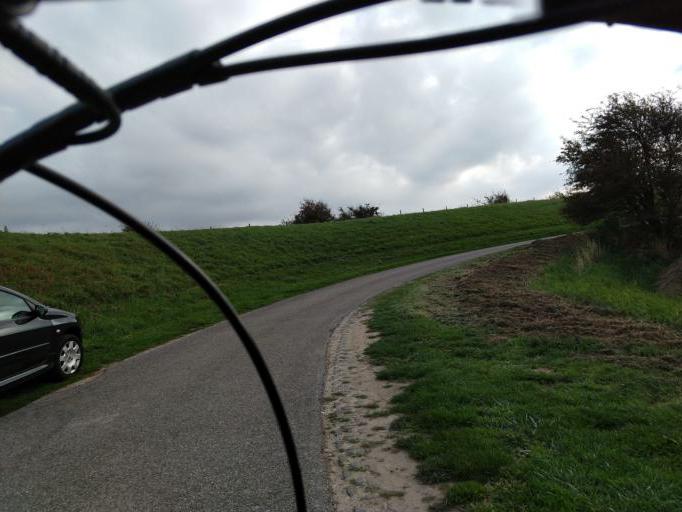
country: NL
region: South Holland
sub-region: Gemeente Goeree-Overflakkee
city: Goedereede
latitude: 51.7162
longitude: 3.9782
